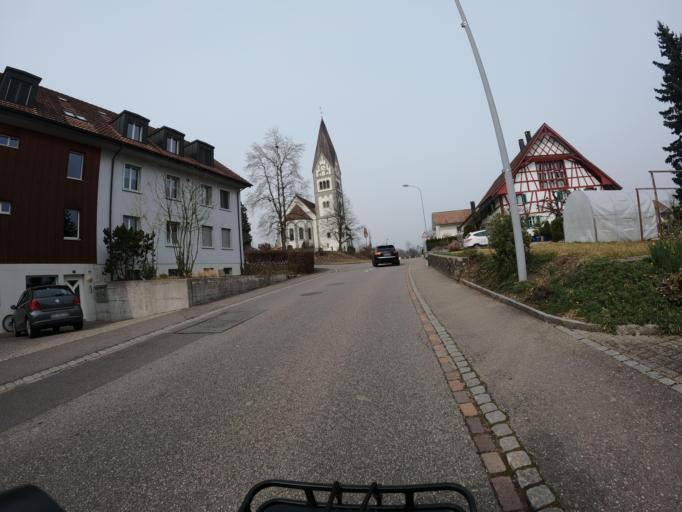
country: CH
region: Aargau
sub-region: Bezirk Baden
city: Mellingen
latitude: 47.4120
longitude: 8.2578
